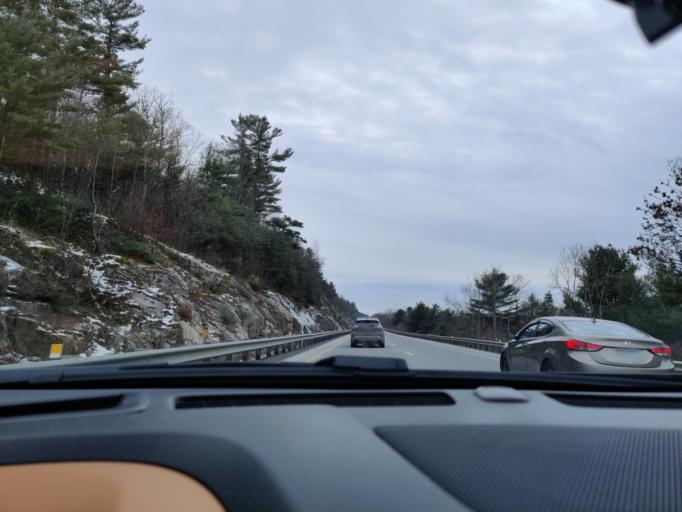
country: US
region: New York
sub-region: Jefferson County
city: Alexandria Bay
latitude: 44.4136
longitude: -75.9233
